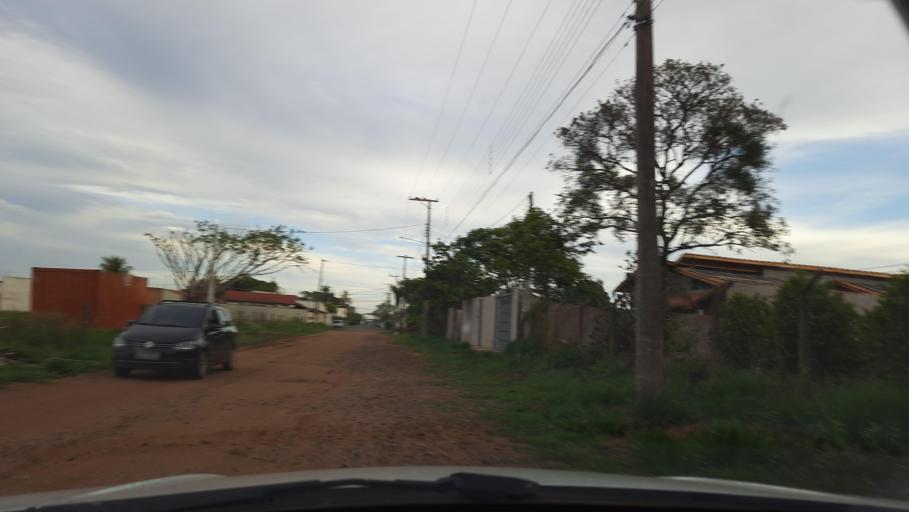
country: BR
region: Sao Paulo
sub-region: Casa Branca
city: Casa Branca
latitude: -21.7789
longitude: -47.0648
